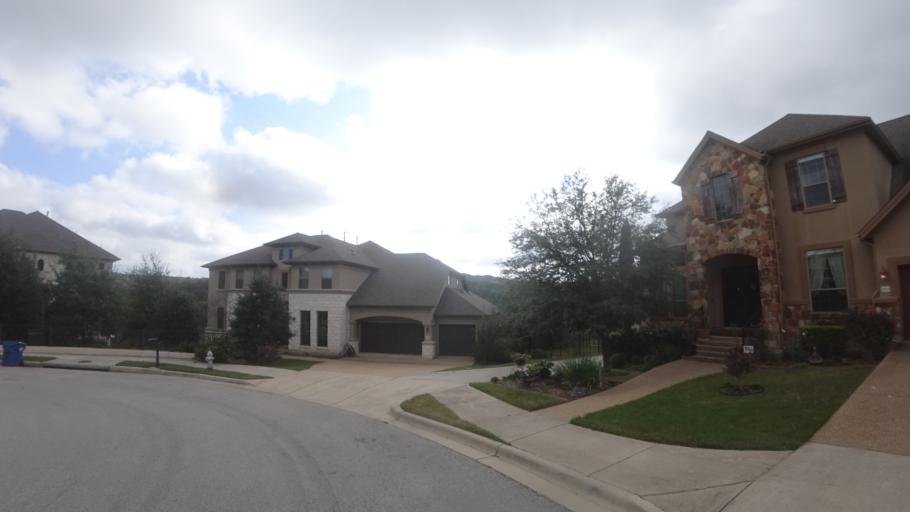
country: US
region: Texas
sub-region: Travis County
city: Barton Creek
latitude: 30.3148
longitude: -97.8952
